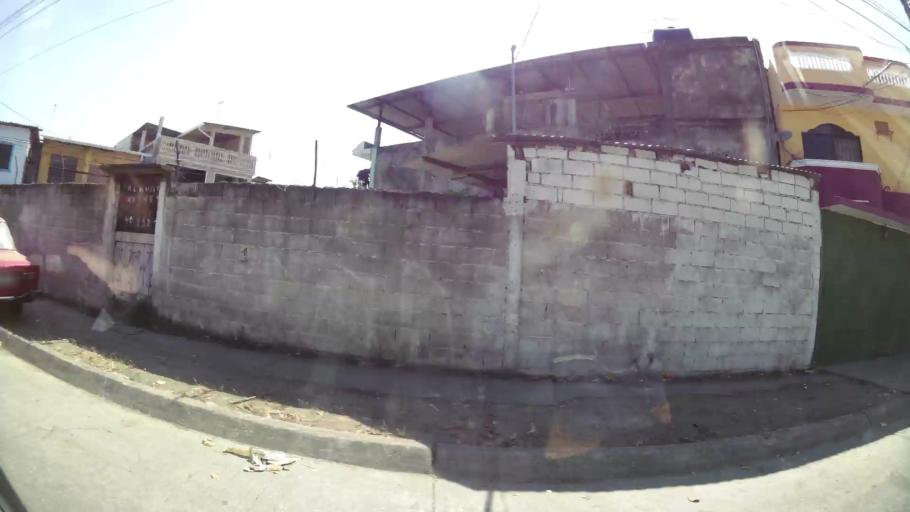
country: EC
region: Guayas
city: Eloy Alfaro
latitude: -2.1224
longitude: -79.8866
